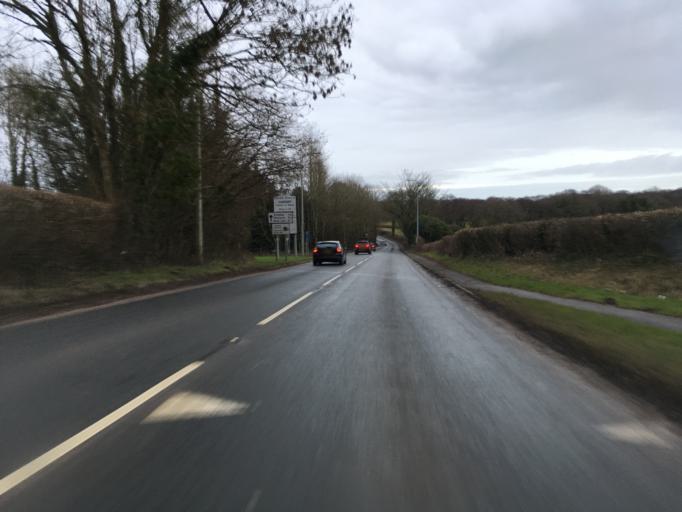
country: GB
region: Wales
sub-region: Rhondda Cynon Taf
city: Llantwit Fardre
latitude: 51.5187
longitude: -3.3359
